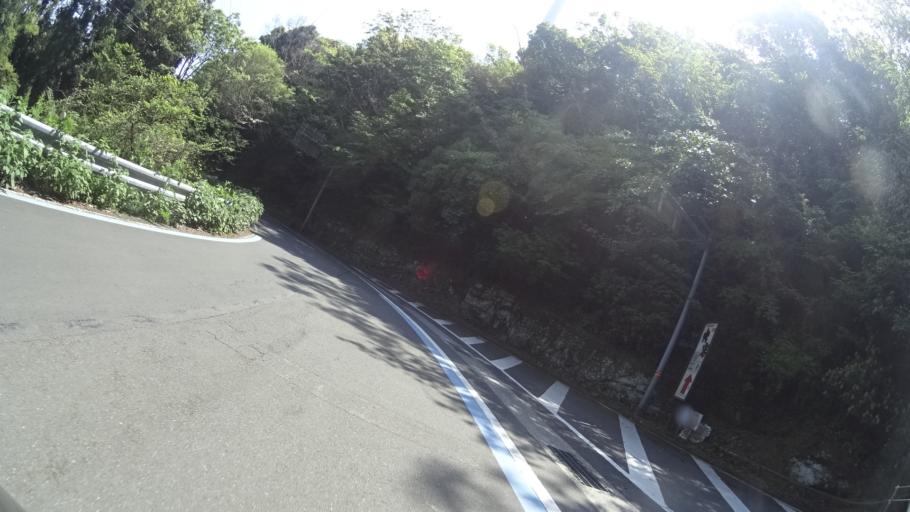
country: JP
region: Ehime
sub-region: Nishiuwa-gun
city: Ikata-cho
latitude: 33.3775
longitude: 132.0640
